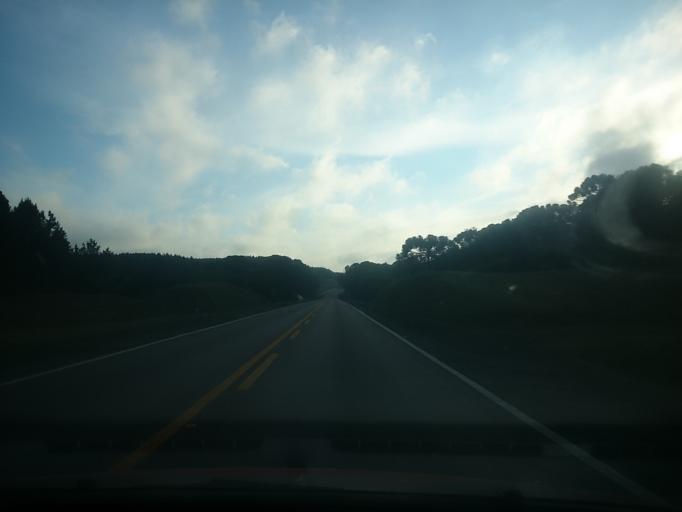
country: BR
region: Rio Grande do Sul
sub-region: Vacaria
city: Estrela
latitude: -28.1263
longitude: -50.6353
